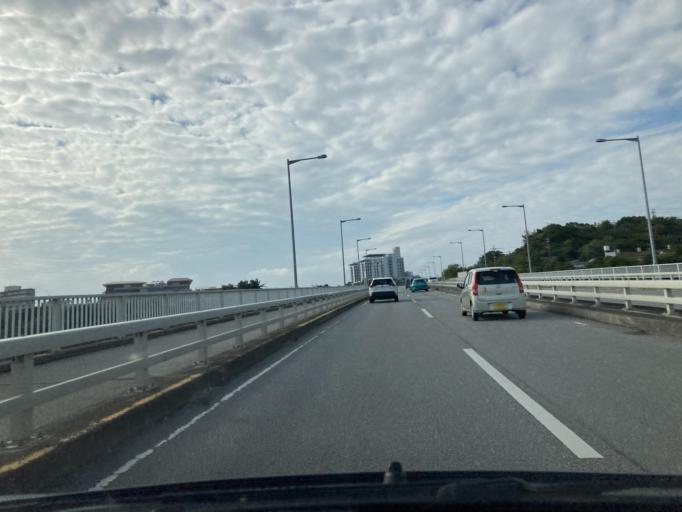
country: JP
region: Okinawa
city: Okinawa
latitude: 26.3147
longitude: 127.8044
